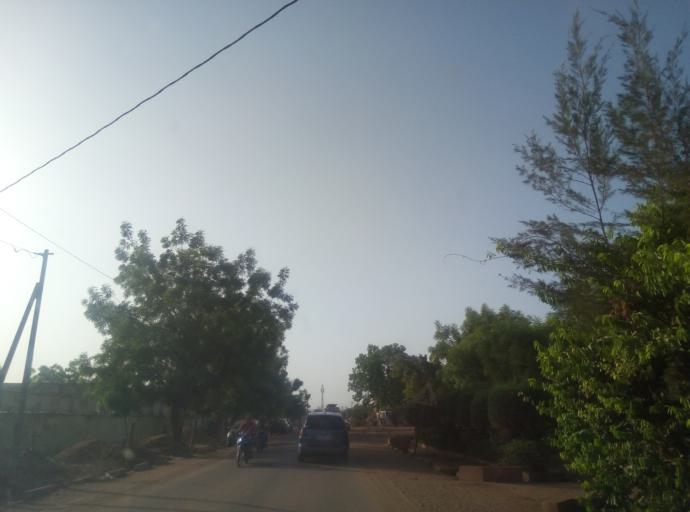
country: ML
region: Bamako
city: Bamako
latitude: 12.6084
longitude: -7.9722
